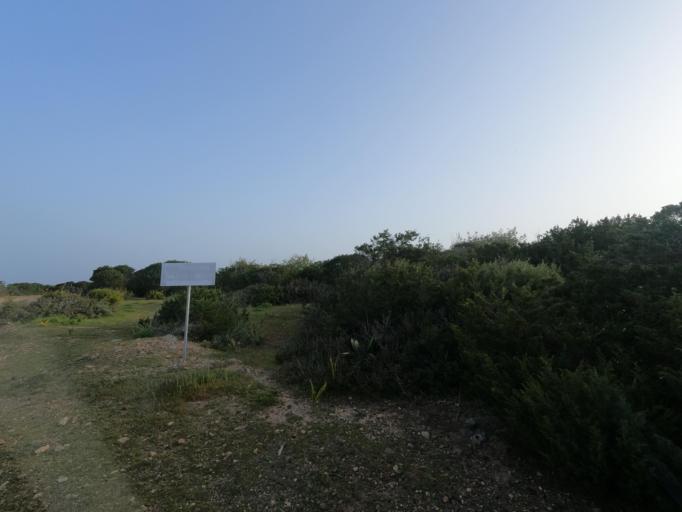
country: CY
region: Pafos
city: Pegeia
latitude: 34.9752
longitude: 32.3142
